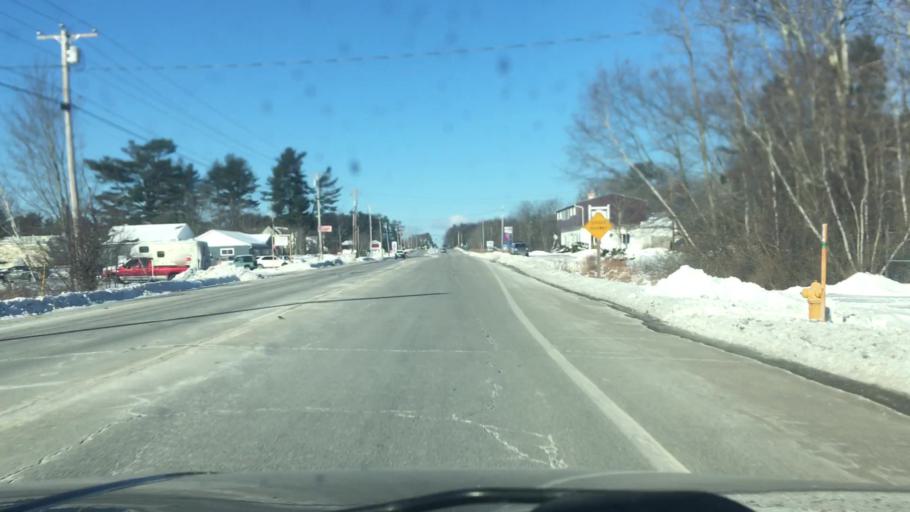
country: US
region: Maine
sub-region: York County
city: South Eliot
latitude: 43.1279
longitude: -70.7684
